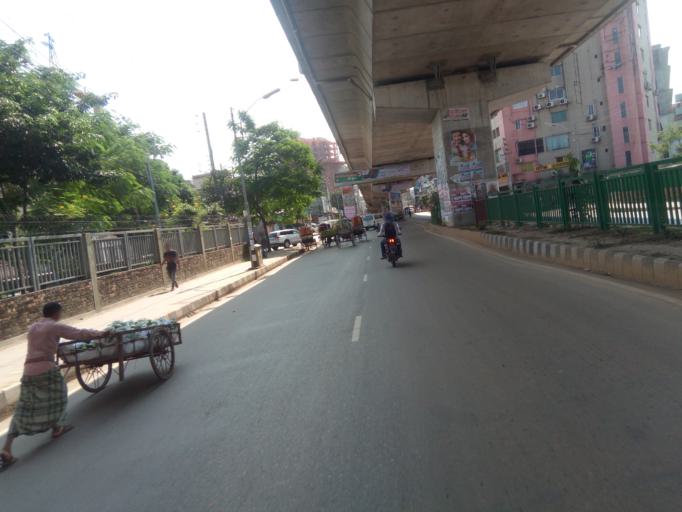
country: BD
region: Dhaka
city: Paltan
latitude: 23.7523
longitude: 90.4016
